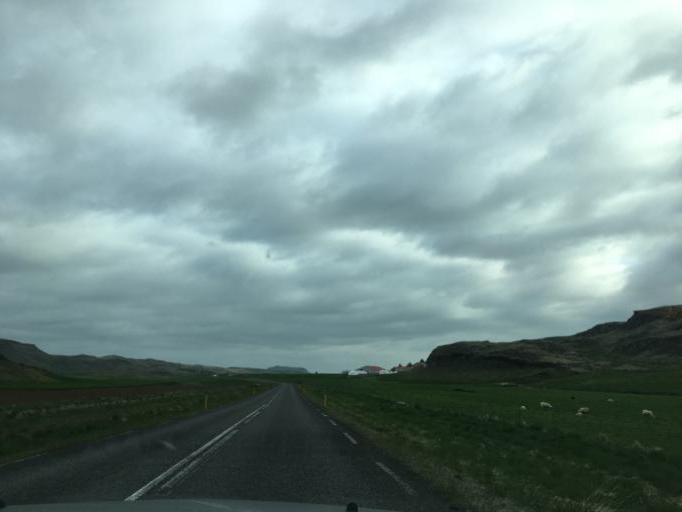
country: IS
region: South
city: Vestmannaeyjar
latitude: 64.2021
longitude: -20.2756
